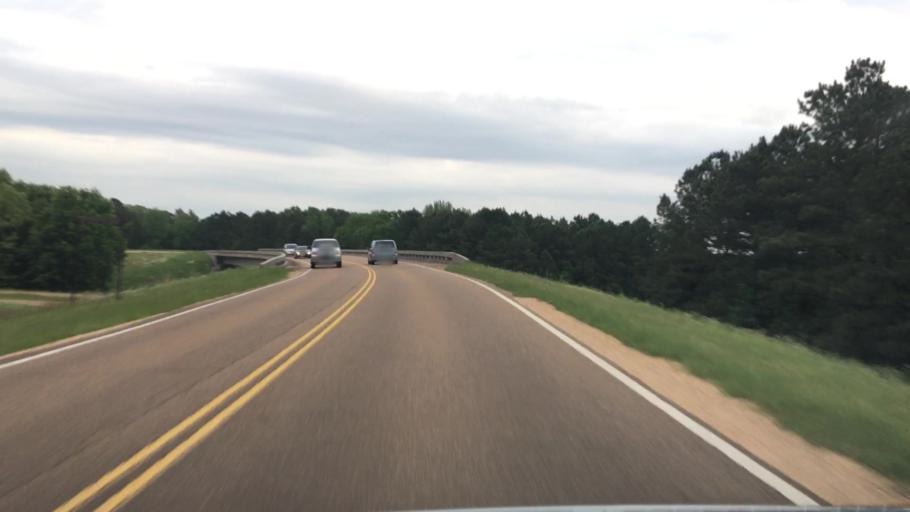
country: US
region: Mississippi
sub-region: Hinds County
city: Clinton
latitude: 32.3809
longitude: -90.2608
